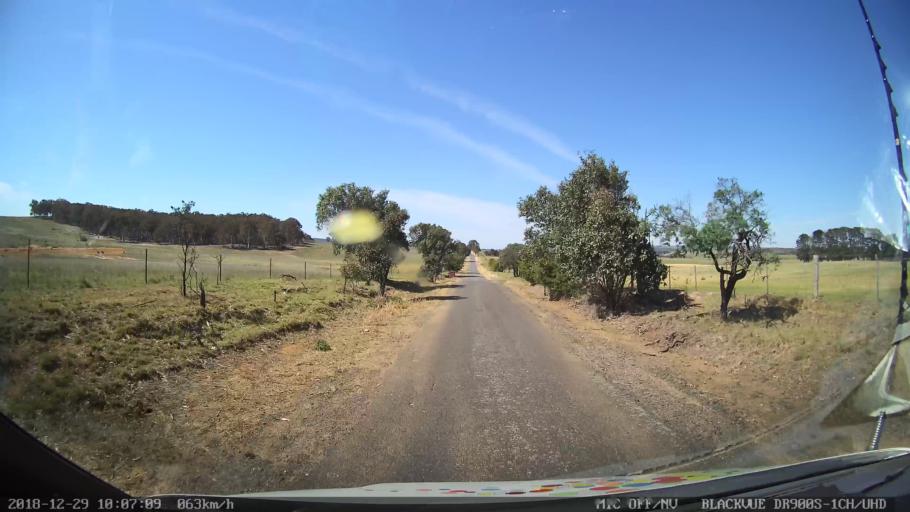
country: AU
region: New South Wales
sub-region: Yass Valley
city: Gundaroo
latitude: -34.8498
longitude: 149.4537
